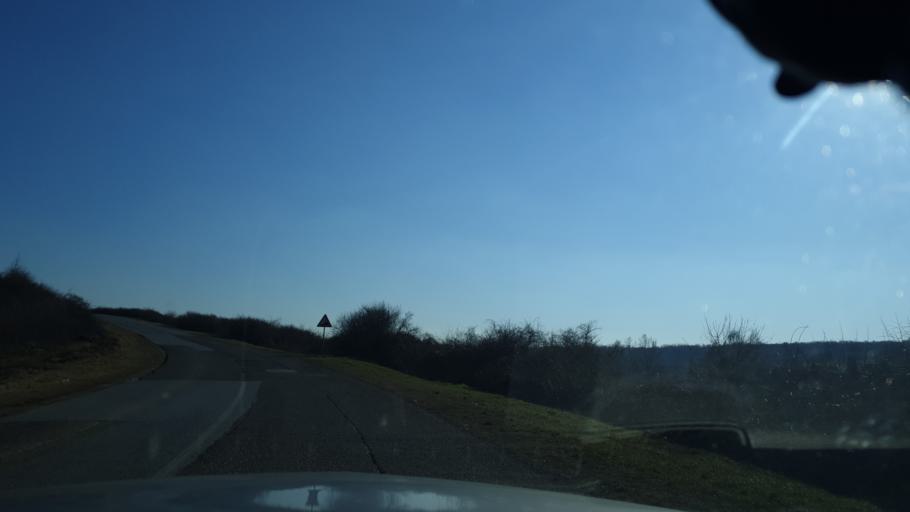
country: RS
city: Vrdnik
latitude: 45.1054
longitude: 19.8008
